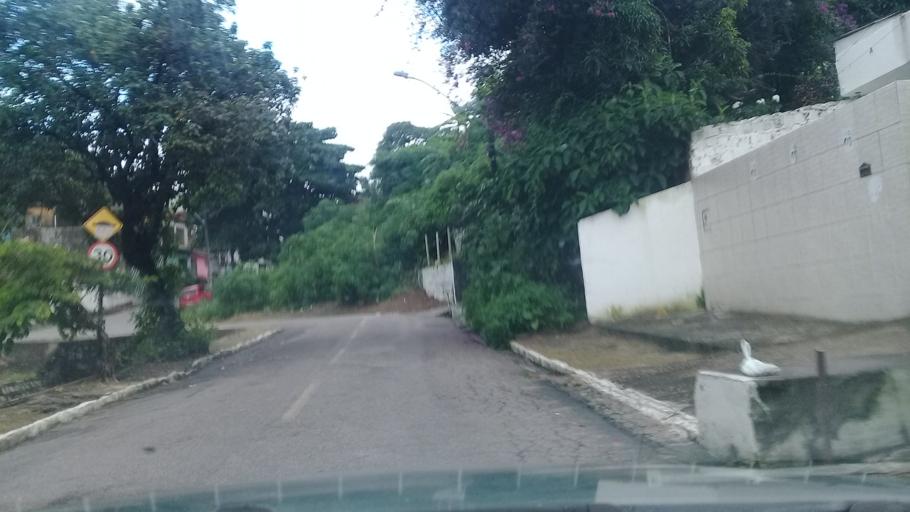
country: BR
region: Pernambuco
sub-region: Jaboatao Dos Guararapes
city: Jaboatao dos Guararapes
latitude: -8.1168
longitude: -34.9519
